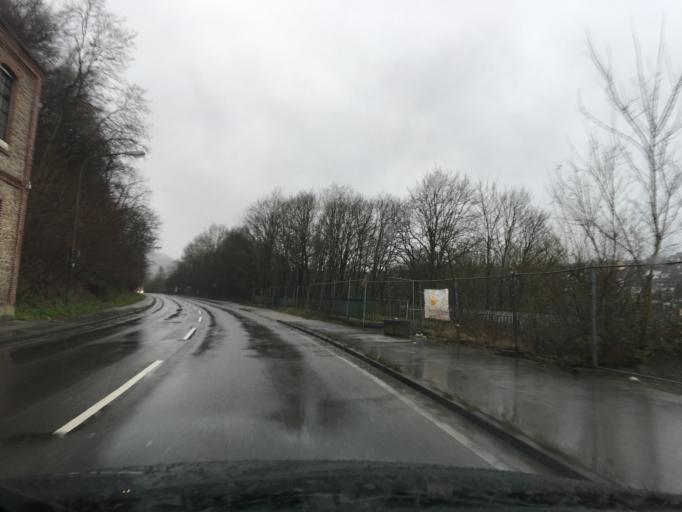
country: DE
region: North Rhine-Westphalia
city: Hattingen
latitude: 51.3598
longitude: 7.1240
